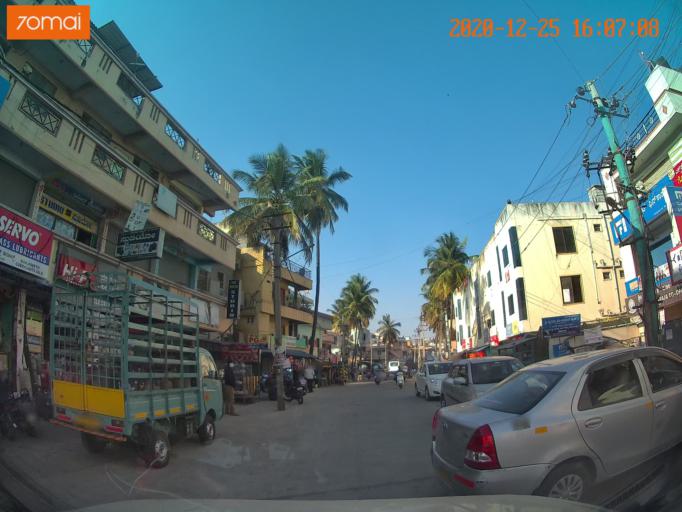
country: IN
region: Karnataka
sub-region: Bangalore Urban
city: Bangalore
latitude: 12.8935
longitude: 77.6258
